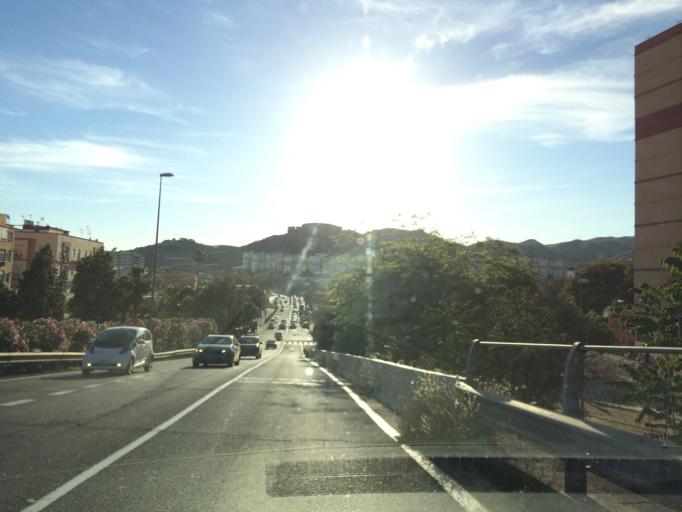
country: ES
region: Andalusia
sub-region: Provincia de Malaga
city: Malaga
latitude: 36.7374
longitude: -4.4210
